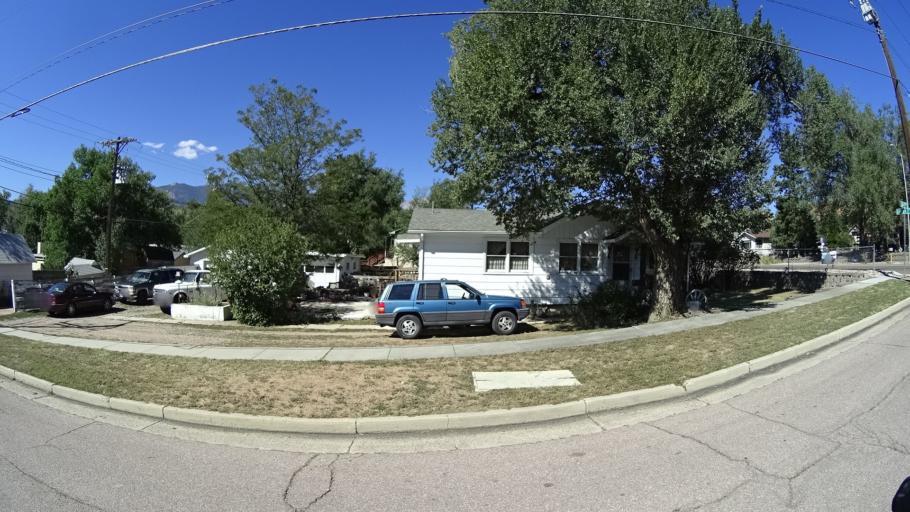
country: US
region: Colorado
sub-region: El Paso County
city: Colorado Springs
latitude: 38.8475
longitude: -104.8519
